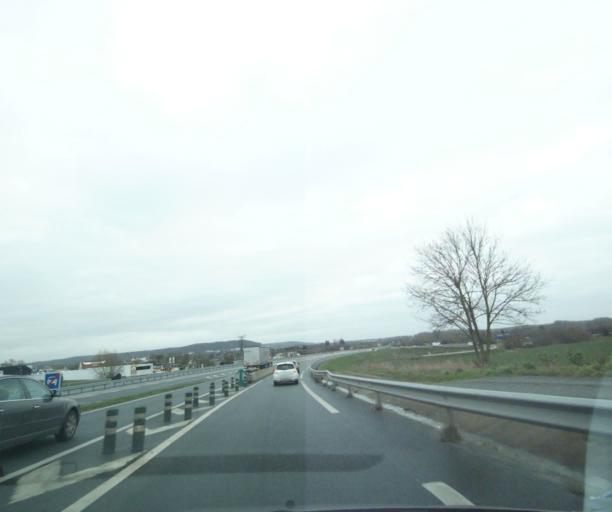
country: FR
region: Picardie
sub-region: Departement de l'Oise
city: Noyon
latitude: 49.5677
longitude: 2.9767
